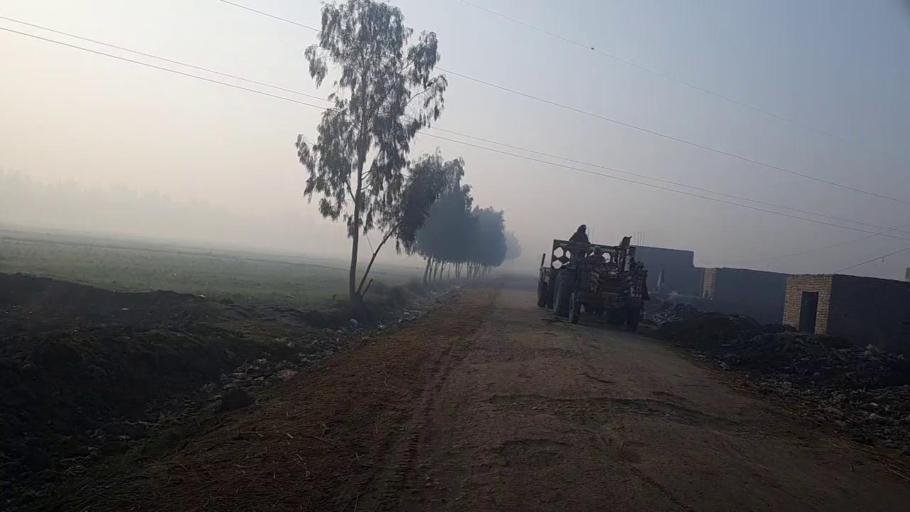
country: PK
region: Sindh
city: Mehar
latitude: 27.1691
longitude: 67.8234
